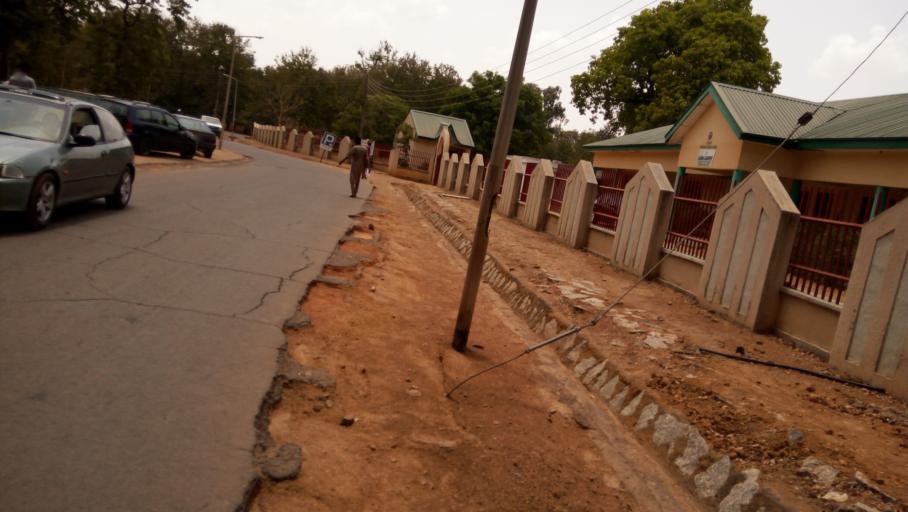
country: NG
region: Kaduna
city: Zaria
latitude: 11.1487
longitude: 7.6530
